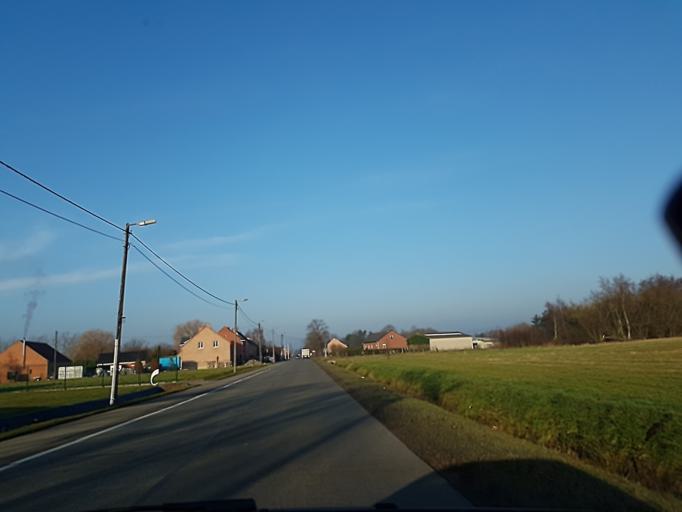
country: BE
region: Flanders
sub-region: Provincie Vlaams-Brabant
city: Tremelo
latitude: 51.0245
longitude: 4.7107
